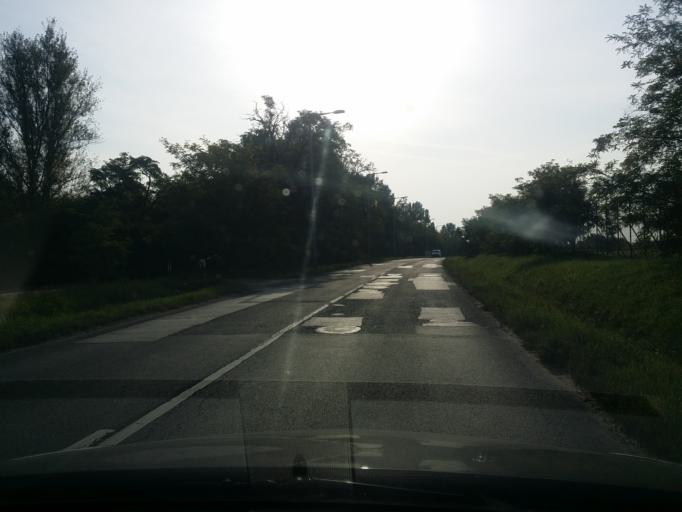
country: HU
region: Budapest
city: Budapest XV. keruelet
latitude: 47.5805
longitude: 19.1401
